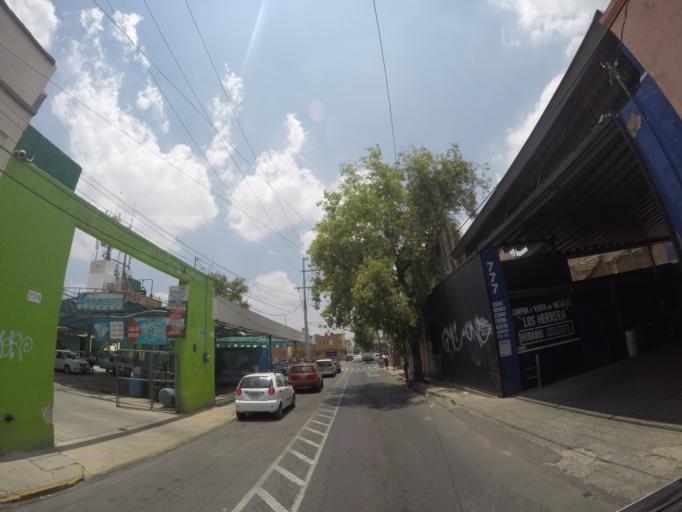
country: MX
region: Jalisco
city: Guadalajara
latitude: 20.6838
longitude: -103.3548
